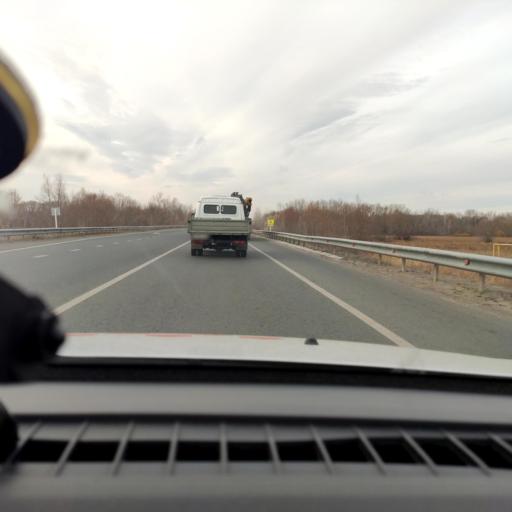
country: RU
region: Samara
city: Novokuybyshevsk
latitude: 53.1407
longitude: 49.9818
